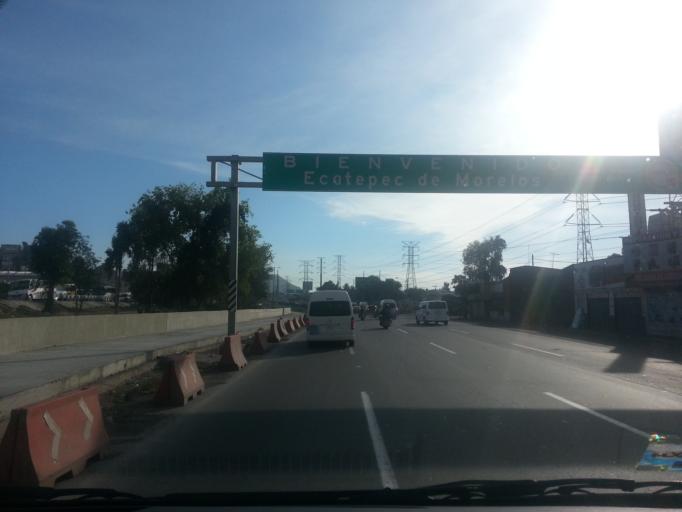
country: MX
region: Mexico
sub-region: Tlalnepantla de Baz
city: Puerto Escondido (Tepeolulco Puerto Escondido)
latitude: 19.5219
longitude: -99.0908
